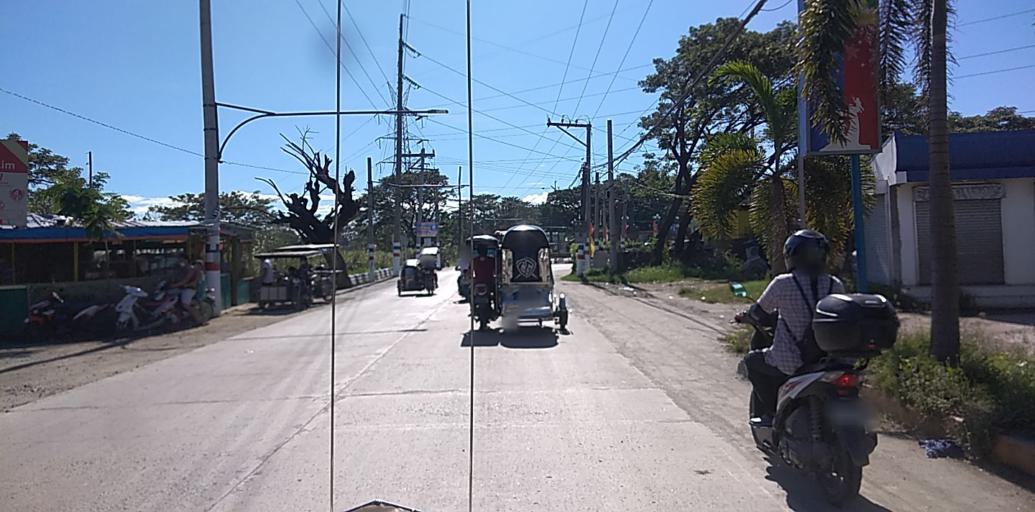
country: PH
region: Central Luzon
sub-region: Province of Pampanga
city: San Luis
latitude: 15.0434
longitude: 120.7892
